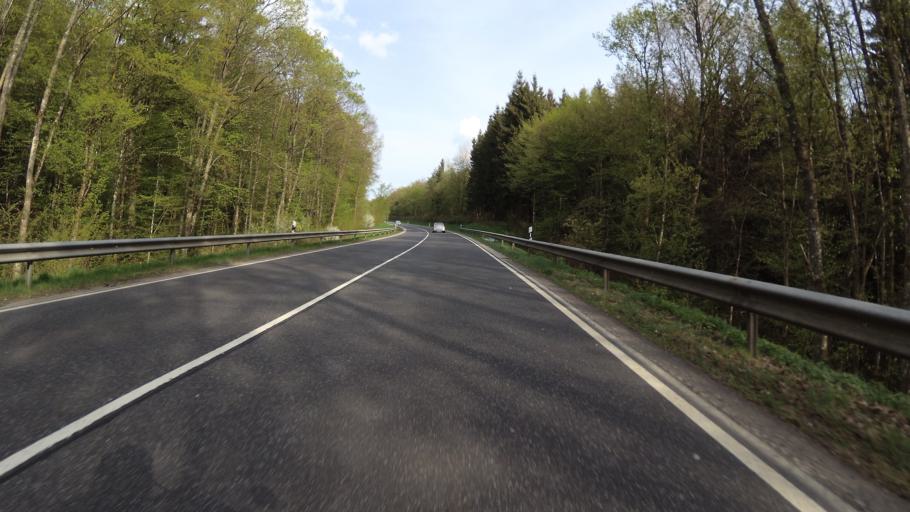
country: DE
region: Rheinland-Pfalz
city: Auderath
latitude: 50.1939
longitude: 6.9910
